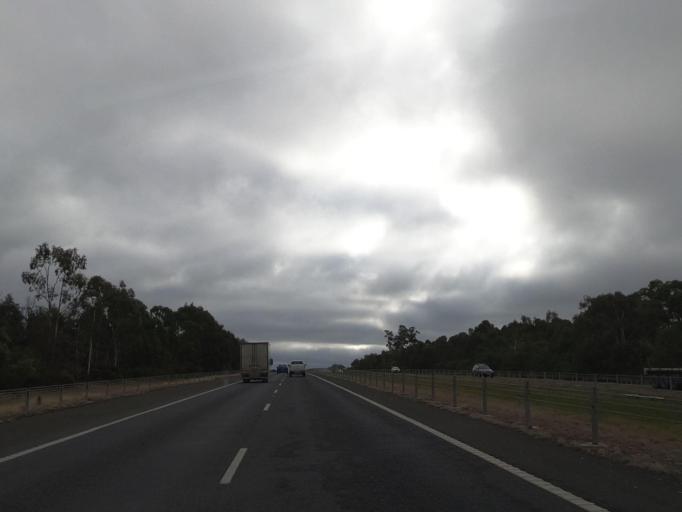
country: AU
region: Victoria
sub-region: Mount Alexander
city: Castlemaine
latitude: -37.0612
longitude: 144.3044
